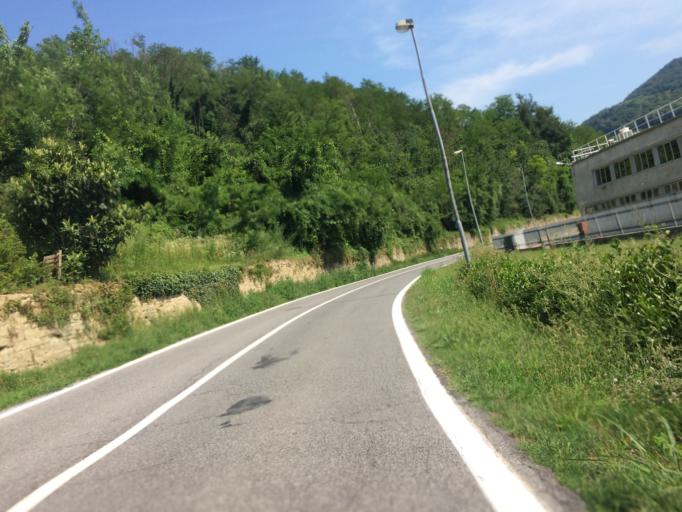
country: IT
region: Piedmont
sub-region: Provincia di Cuneo
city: Cortemilia
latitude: 44.5817
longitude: 8.1854
